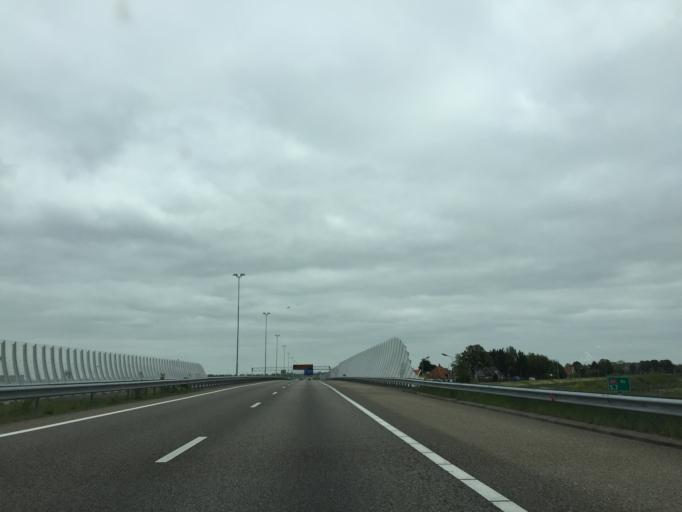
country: NL
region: North Holland
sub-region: Gemeente Haarlemmermeer
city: Hoofddorp
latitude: 52.3338
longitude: 4.7346
